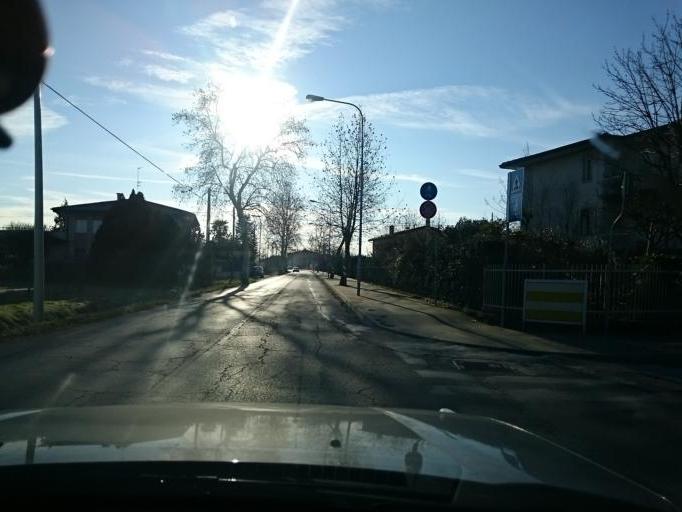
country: IT
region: Veneto
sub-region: Provincia di Padova
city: Montegrotto Terme
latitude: 45.3343
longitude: 11.7951
